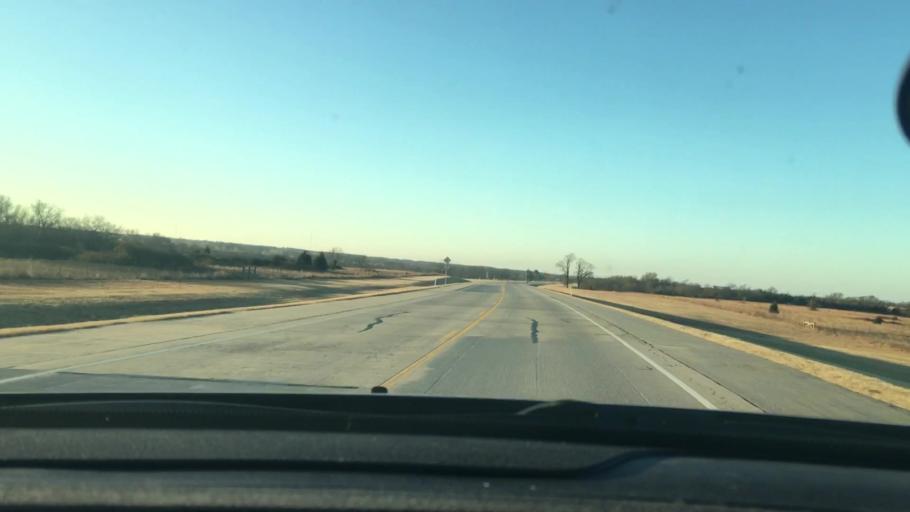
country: US
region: Oklahoma
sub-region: Murray County
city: Sulphur
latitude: 34.5762
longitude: -96.9247
